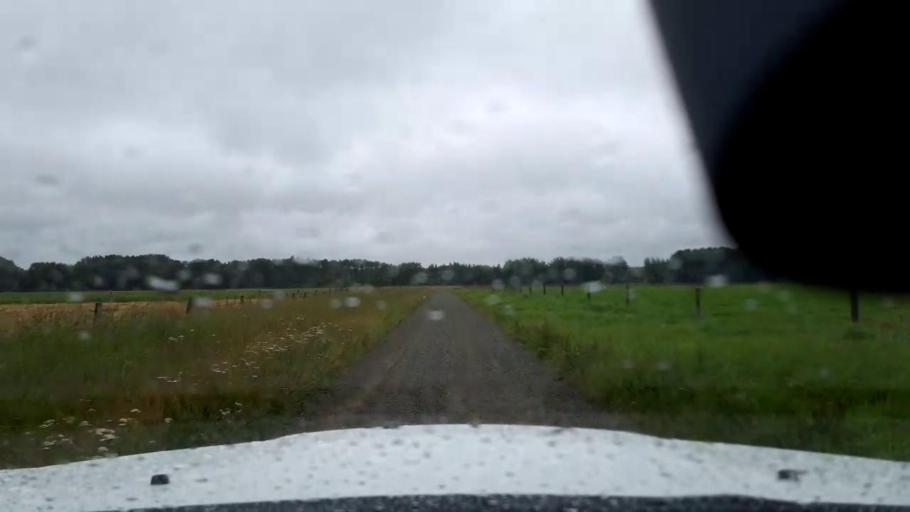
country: NZ
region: Canterbury
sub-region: Timaru District
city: Pleasant Point
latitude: -44.2548
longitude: 171.1998
